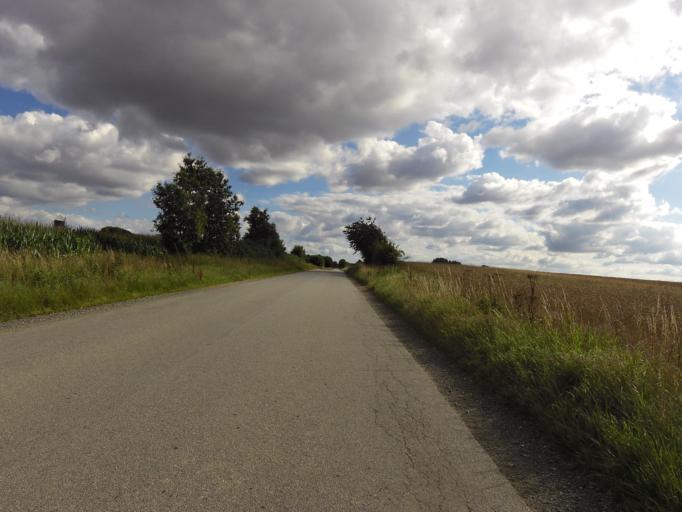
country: DK
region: South Denmark
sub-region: Haderslev Kommune
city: Haderslev
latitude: 55.2176
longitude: 9.4437
